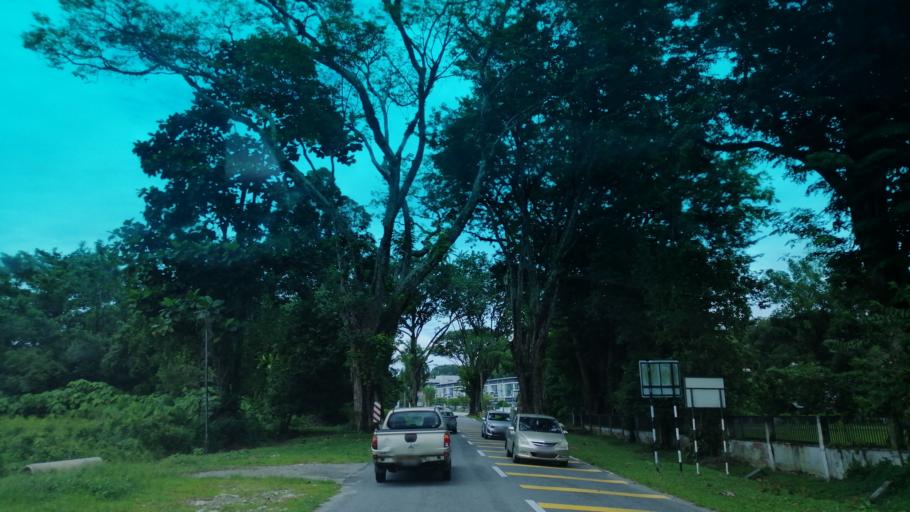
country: MY
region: Perak
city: Taiping
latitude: 4.8583
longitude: 100.7386
